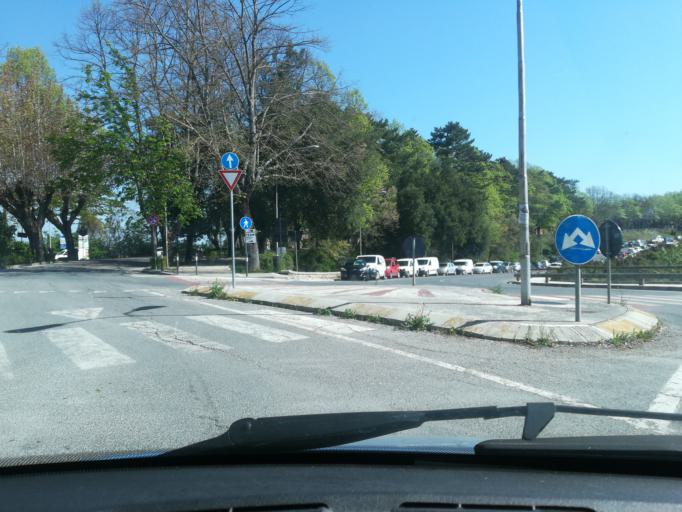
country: IT
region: The Marches
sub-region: Provincia di Macerata
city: Cingoli
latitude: 43.3749
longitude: 13.2090
